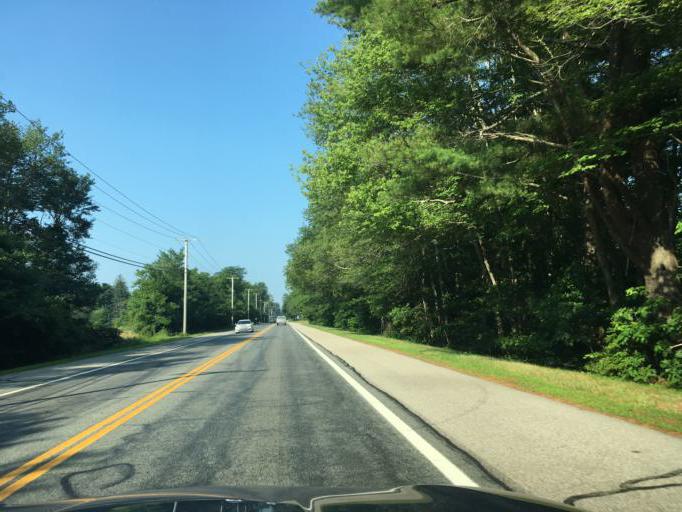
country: US
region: Rhode Island
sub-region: Washington County
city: Kingston
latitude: 41.4974
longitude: -71.5665
